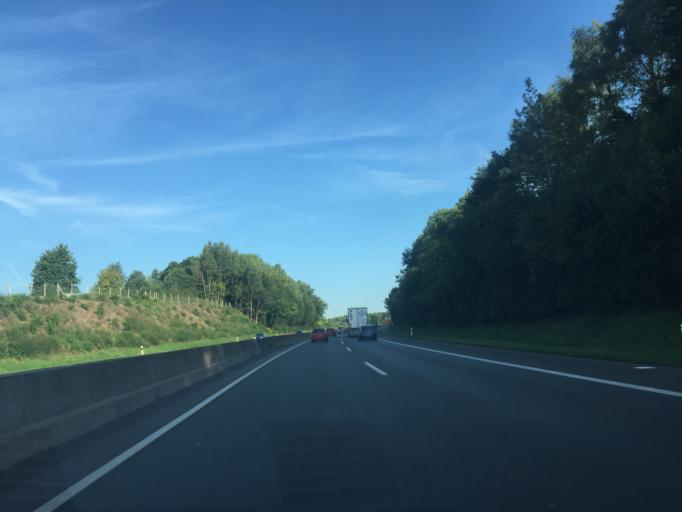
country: DE
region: North Rhine-Westphalia
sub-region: Regierungsbezirk Arnsberg
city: Wenden
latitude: 50.9517
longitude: 7.8562
